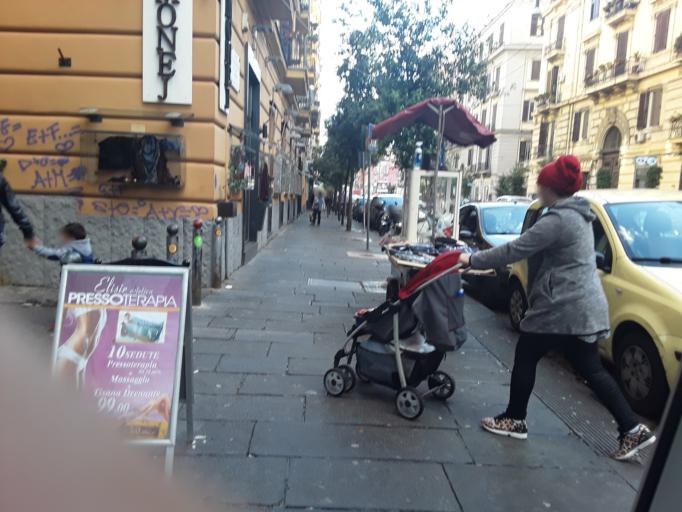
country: IT
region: Campania
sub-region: Provincia di Napoli
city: Napoli
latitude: 40.8573
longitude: 14.2673
